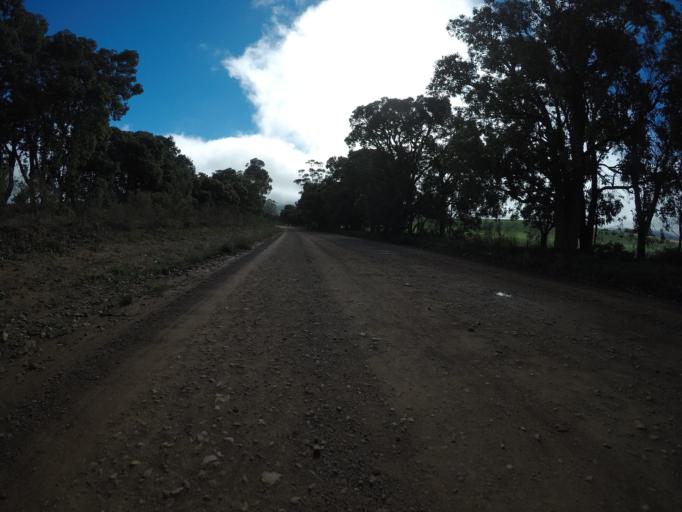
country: ZA
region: Western Cape
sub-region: Cape Winelands District Municipality
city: Ashton
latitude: -34.1149
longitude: 19.8041
